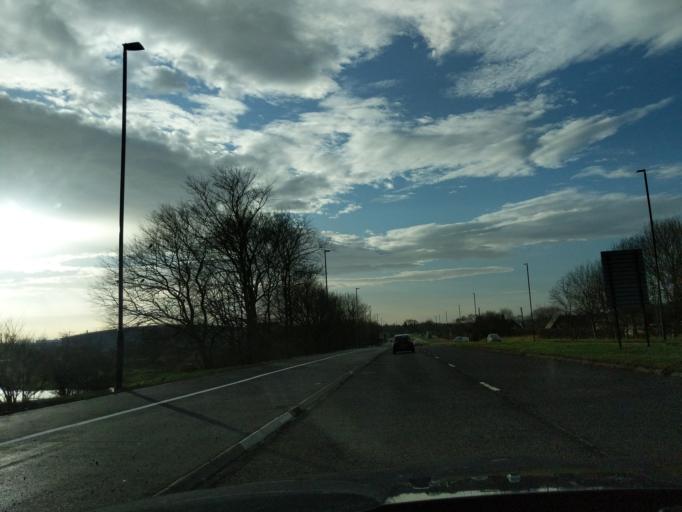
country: GB
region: England
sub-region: Newcastle upon Tyne
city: Gosforth
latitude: 55.0211
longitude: -1.5958
